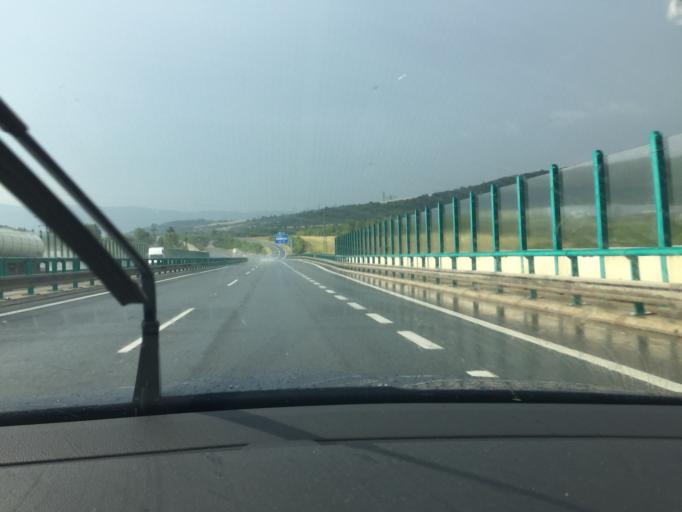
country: CZ
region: Ustecky
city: Trmice
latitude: 50.6610
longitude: 13.9800
